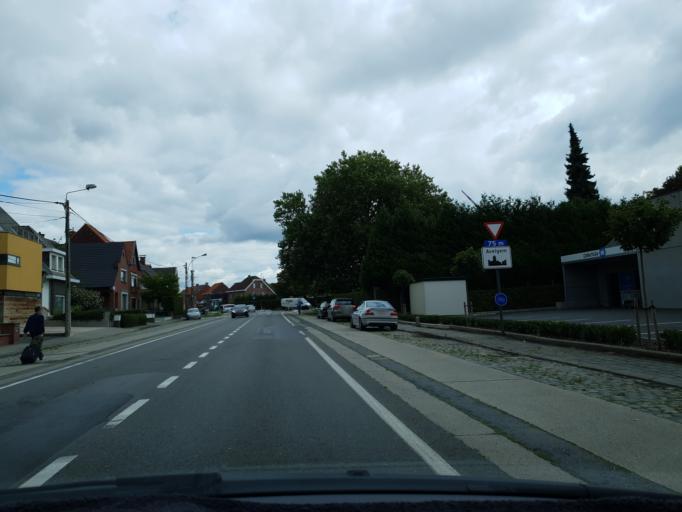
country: BE
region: Flanders
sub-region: Provincie West-Vlaanderen
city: Avelgem
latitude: 50.7645
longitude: 3.4393
